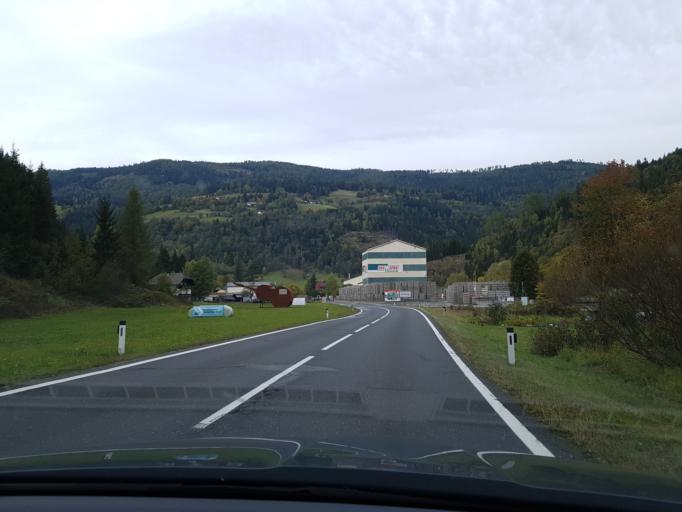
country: AT
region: Salzburg
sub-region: Politischer Bezirk Tamsweg
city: Ramingstein
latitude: 47.0751
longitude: 13.8218
